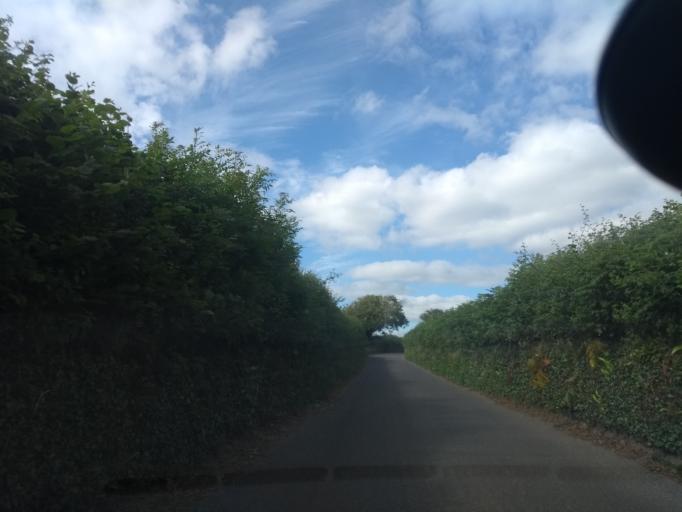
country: GB
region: England
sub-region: Devon
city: Modbury
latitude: 50.3009
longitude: -3.8887
